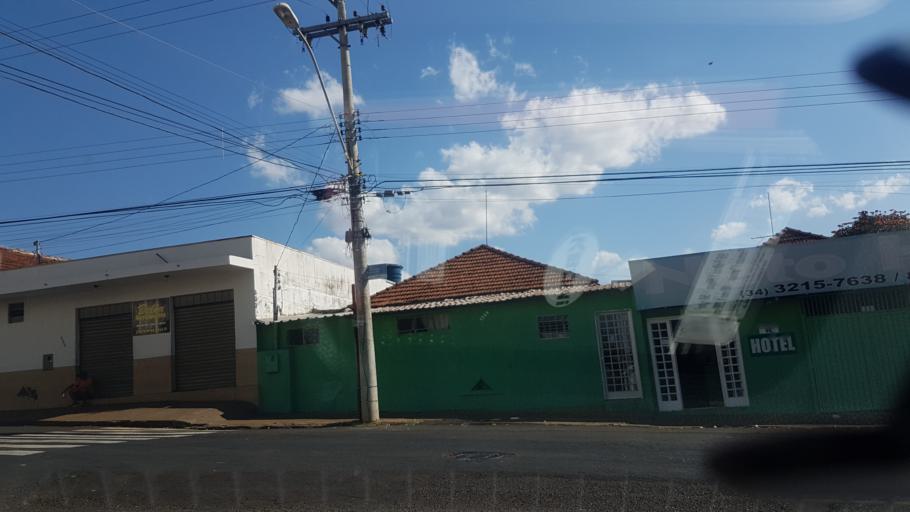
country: BR
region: Minas Gerais
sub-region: Uberlandia
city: Uberlandia
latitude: -18.9065
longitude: -48.2861
